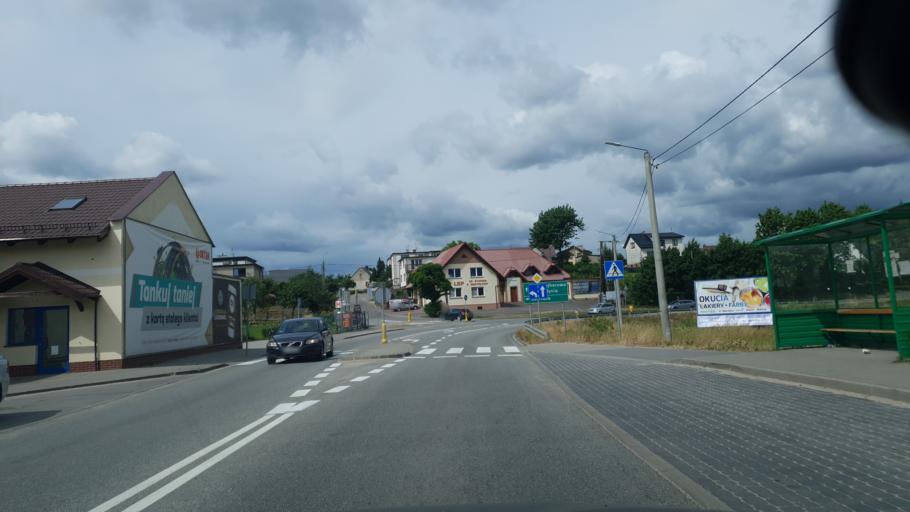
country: PL
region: Pomeranian Voivodeship
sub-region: Powiat kartuski
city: Kartuzy
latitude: 54.3519
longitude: 18.2180
